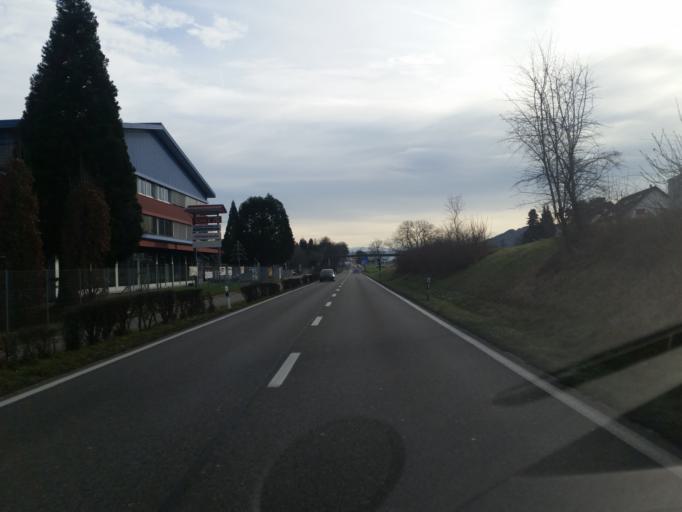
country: CH
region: Aargau
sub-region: Bezirk Bremgarten
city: Villmergen
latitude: 47.3546
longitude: 8.2491
